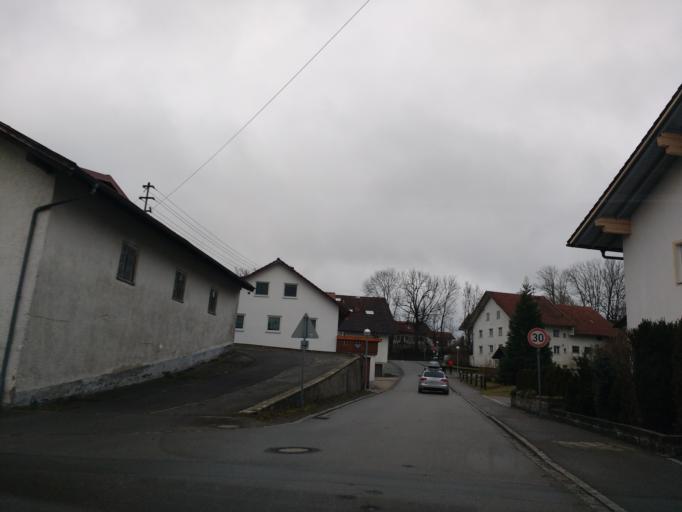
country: DE
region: Bavaria
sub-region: Swabia
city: Betzigau
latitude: 47.7365
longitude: 10.3527
